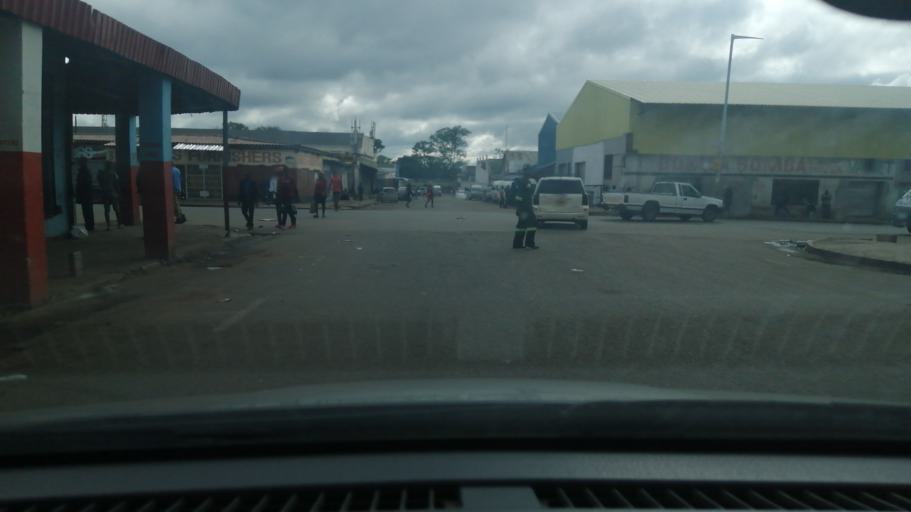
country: ZW
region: Harare
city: Harare
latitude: -17.8395
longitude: 31.0437
